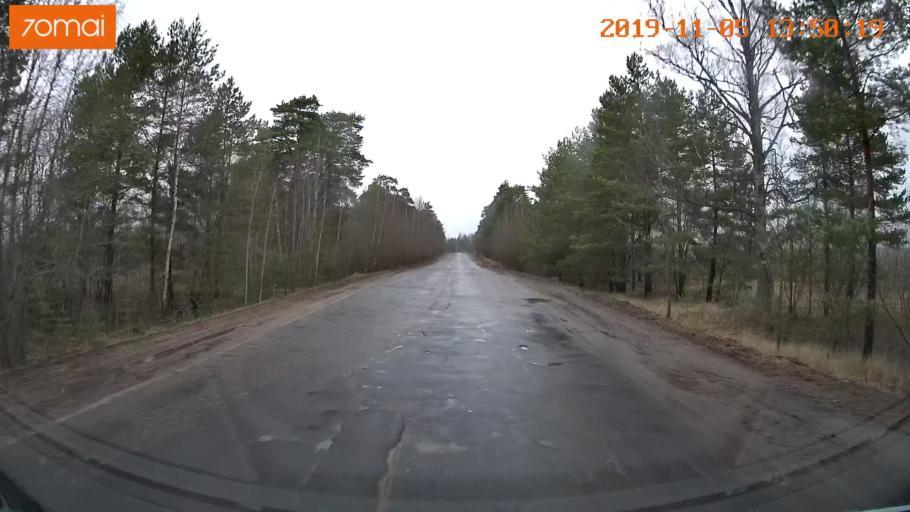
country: RU
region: Ivanovo
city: Kaminskiy
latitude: 57.0185
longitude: 41.4085
